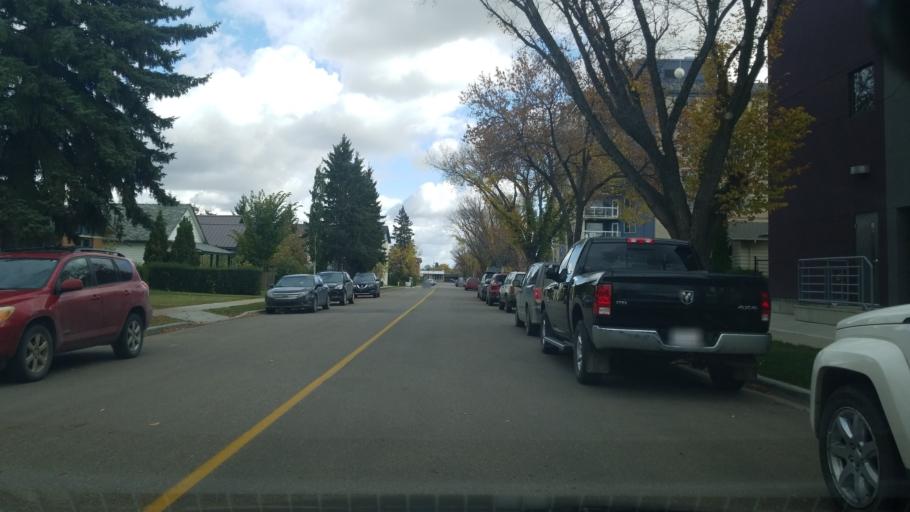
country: CA
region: Saskatchewan
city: Lloydminster
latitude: 53.2807
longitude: -110.0102
